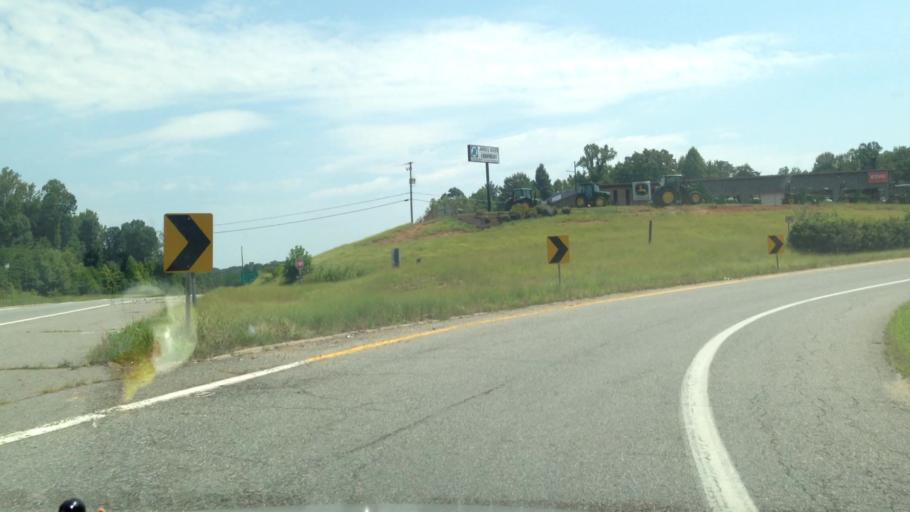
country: US
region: Virginia
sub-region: Henry County
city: Horse Pasture
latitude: 36.6491
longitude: -79.9142
